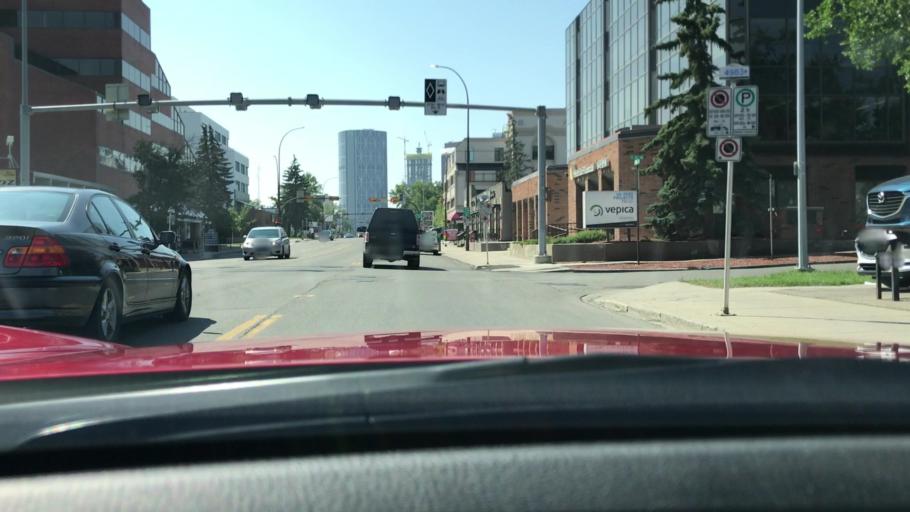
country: CA
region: Alberta
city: Calgary
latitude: 51.0626
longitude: -114.0626
